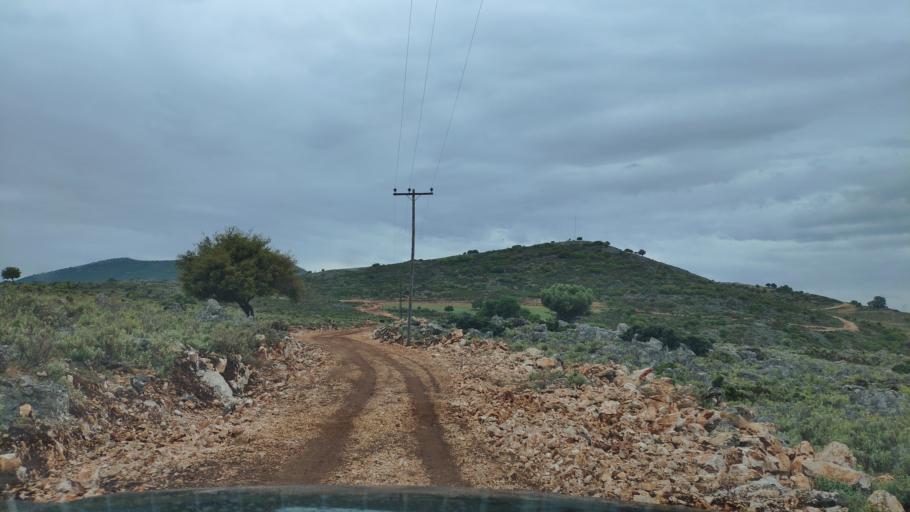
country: GR
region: West Greece
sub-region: Nomos Aitolias kai Akarnanias
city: Archontochorion
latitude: 38.6849
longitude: 21.0289
